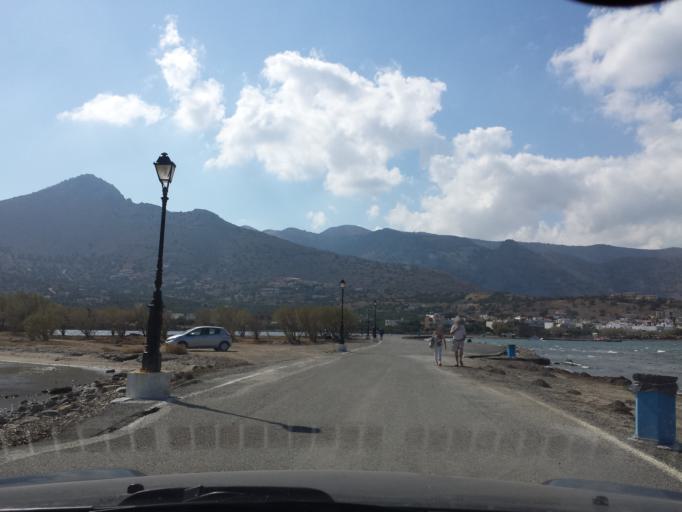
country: GR
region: Crete
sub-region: Nomos Lasithiou
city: Skhisma
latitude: 35.2572
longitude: 25.7341
